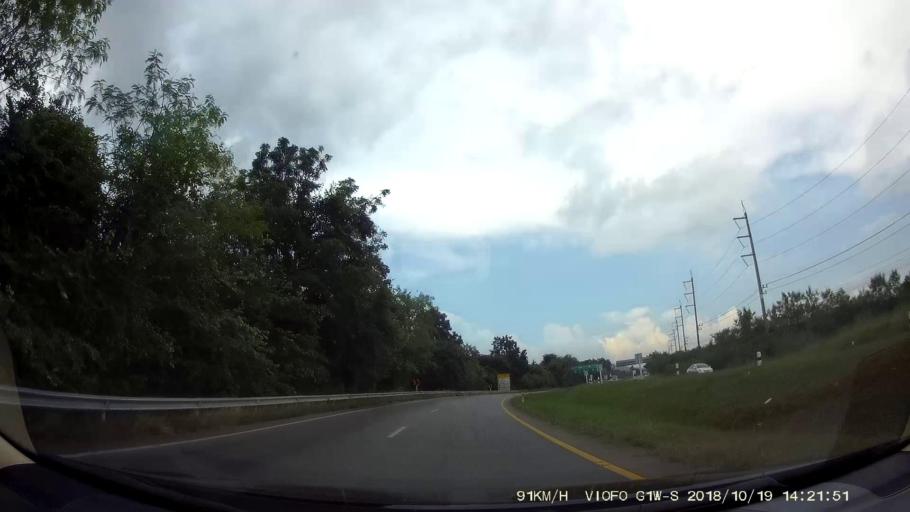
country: TH
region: Chaiyaphum
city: Kaeng Khro
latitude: 16.0568
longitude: 102.2704
